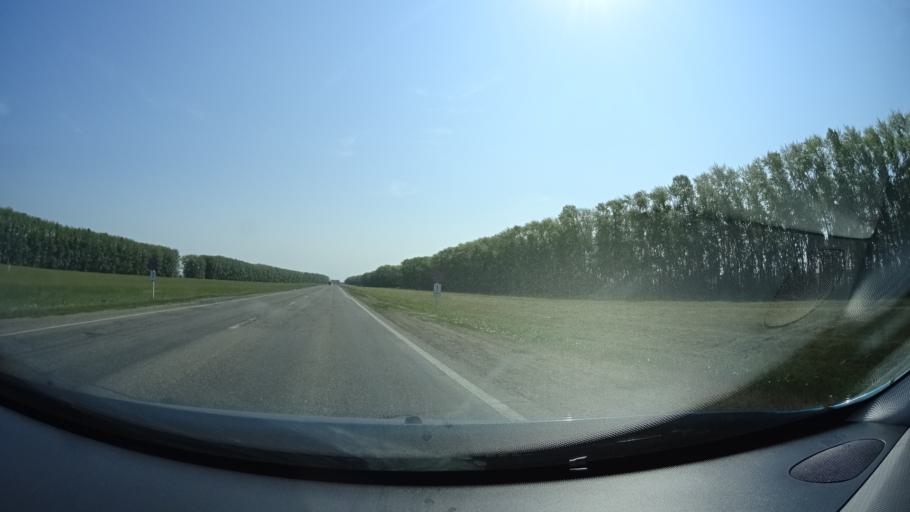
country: RU
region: Bashkortostan
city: Karmaskaly
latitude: 54.3955
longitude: 56.1084
